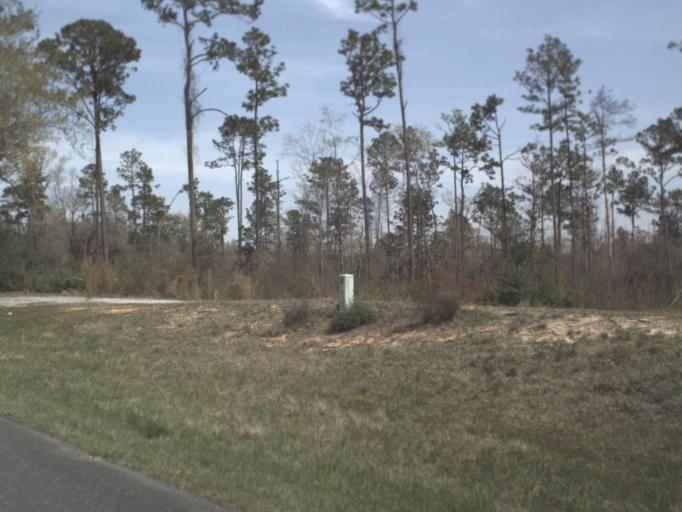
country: US
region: Florida
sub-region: Walton County
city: DeFuniak Springs
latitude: 30.7525
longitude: -85.9590
